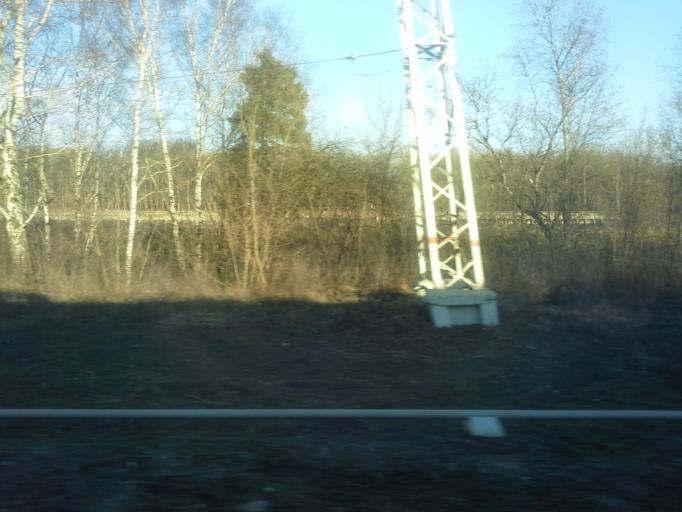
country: RU
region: Moskovskaya
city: Iksha
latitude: 56.1716
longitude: 37.5094
